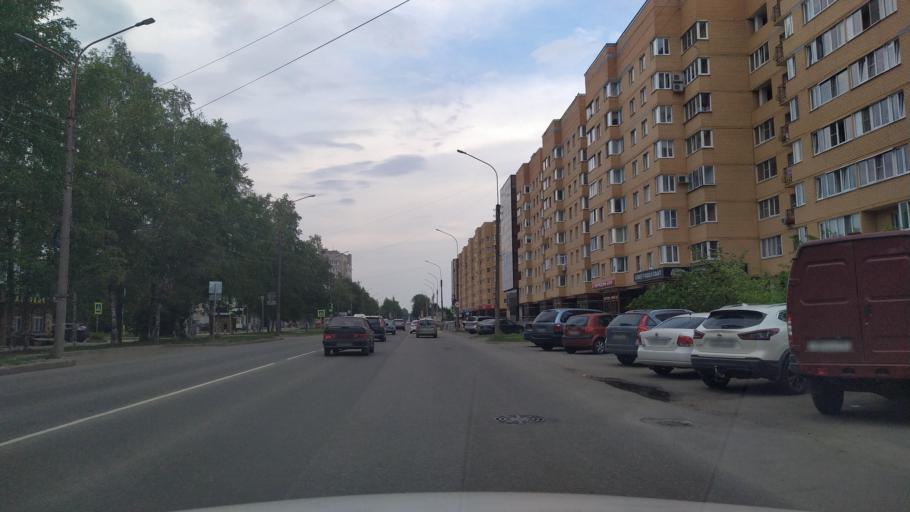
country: RU
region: Novgorod
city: Velikiy Novgorod
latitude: 58.5142
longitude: 31.2427
